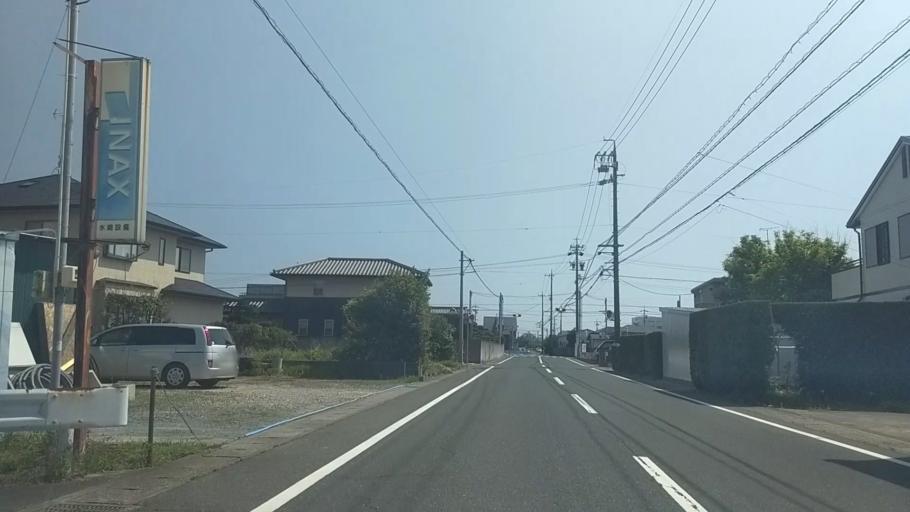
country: JP
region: Shizuoka
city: Hamamatsu
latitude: 34.6734
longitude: 137.7161
